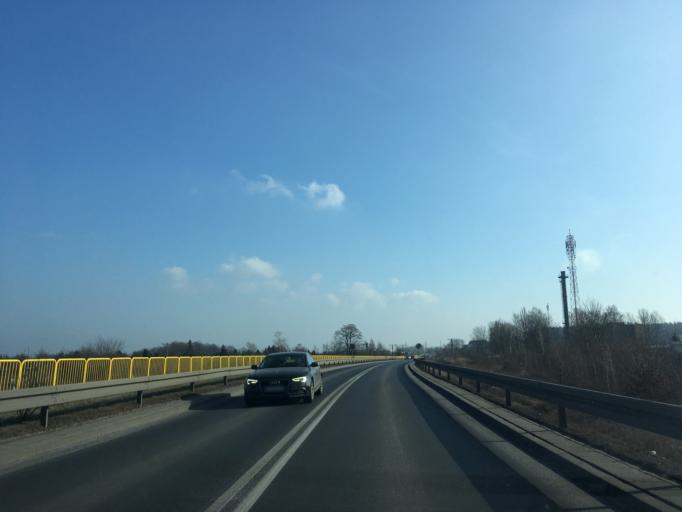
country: PL
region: Lower Silesian Voivodeship
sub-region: Powiat boleslawiecki
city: Boleslawiec
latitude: 51.2670
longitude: 15.5861
